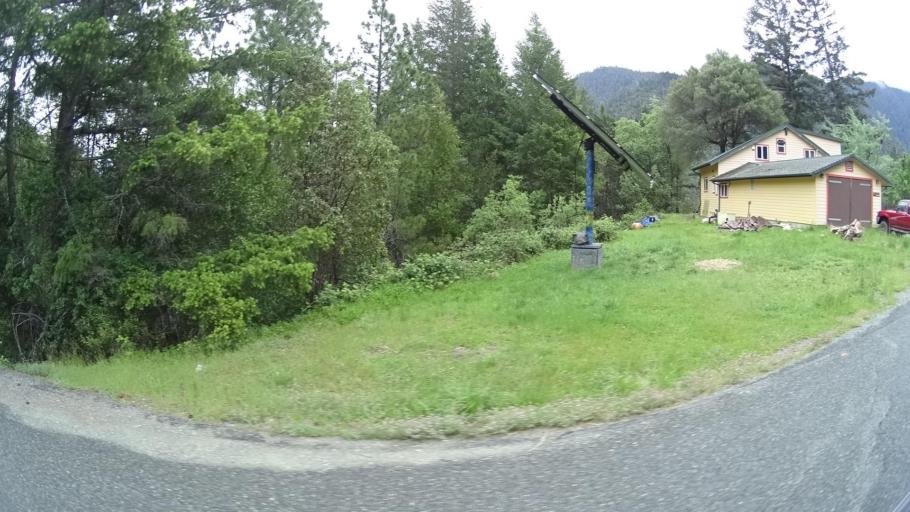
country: US
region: California
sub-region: Humboldt County
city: Willow Creek
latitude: 41.3586
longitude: -123.5070
